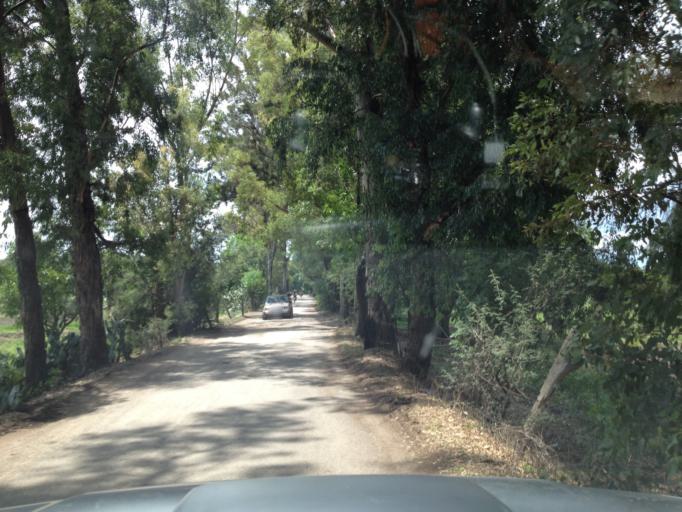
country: MX
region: Michoacan
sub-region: Tarimbaro
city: El Colegio
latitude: 19.7801
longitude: -101.1783
